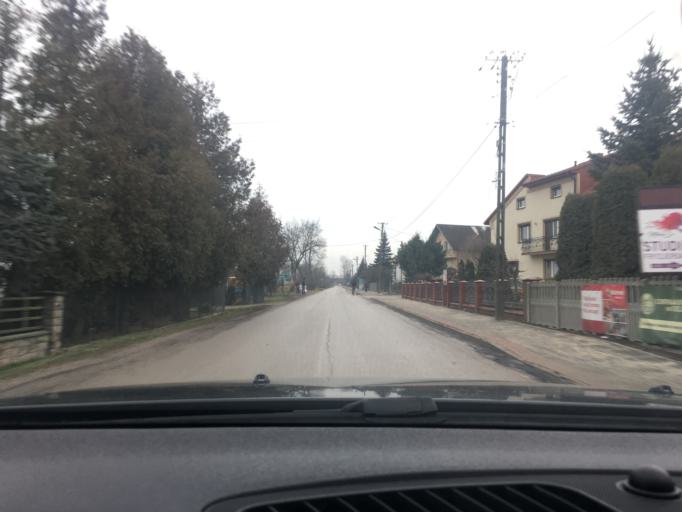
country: PL
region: Swietokrzyskie
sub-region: Powiat jedrzejowski
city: Jedrzejow
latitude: 50.6420
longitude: 20.3854
